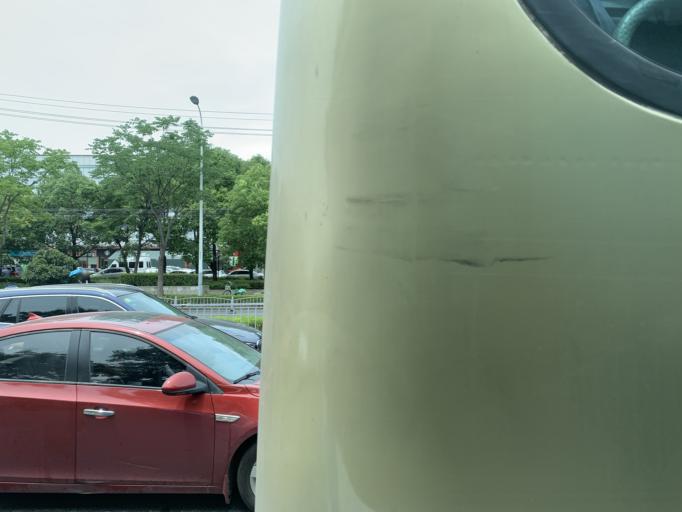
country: CN
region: Shanghai Shi
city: Kangqiao
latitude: 31.1566
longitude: 121.5606
